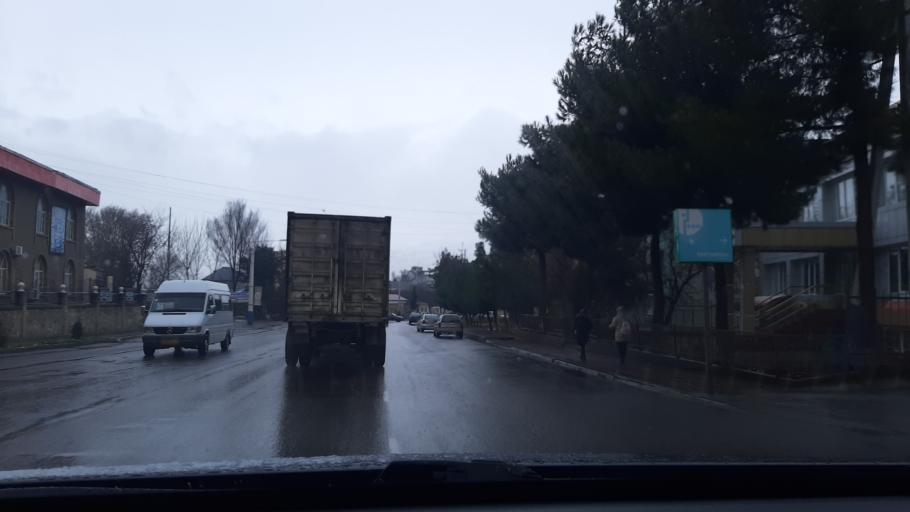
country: TJ
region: Viloyati Sughd
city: Khujand
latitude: 40.2736
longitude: 69.6420
